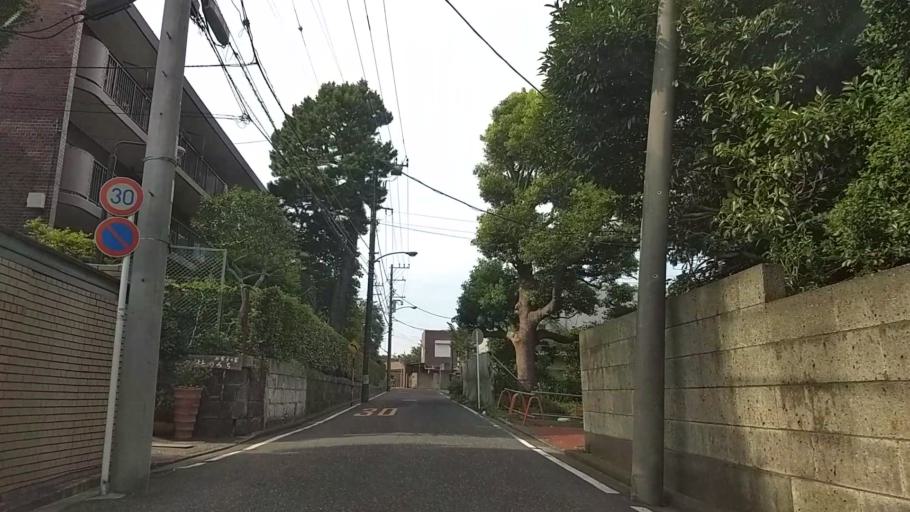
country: JP
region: Kanagawa
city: Yokohama
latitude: 35.4335
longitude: 139.6607
